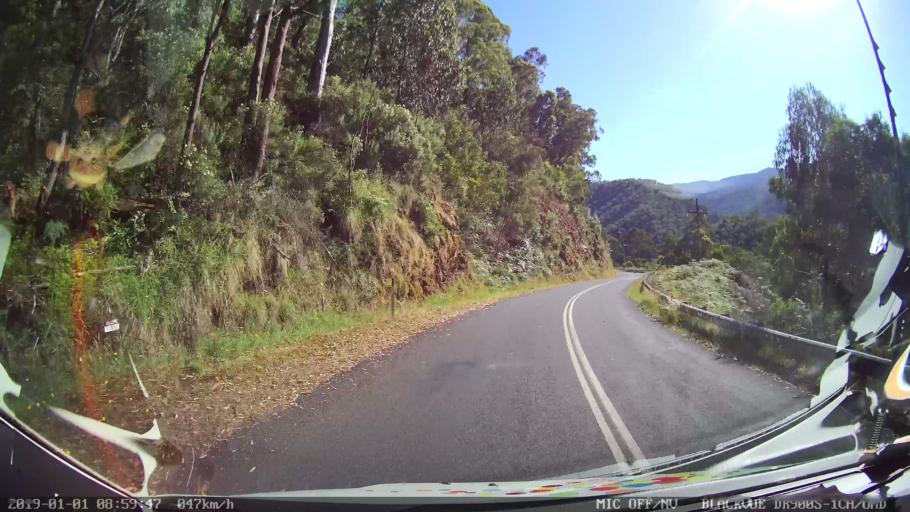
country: AU
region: New South Wales
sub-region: Snowy River
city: Jindabyne
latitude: -36.2389
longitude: 148.1791
